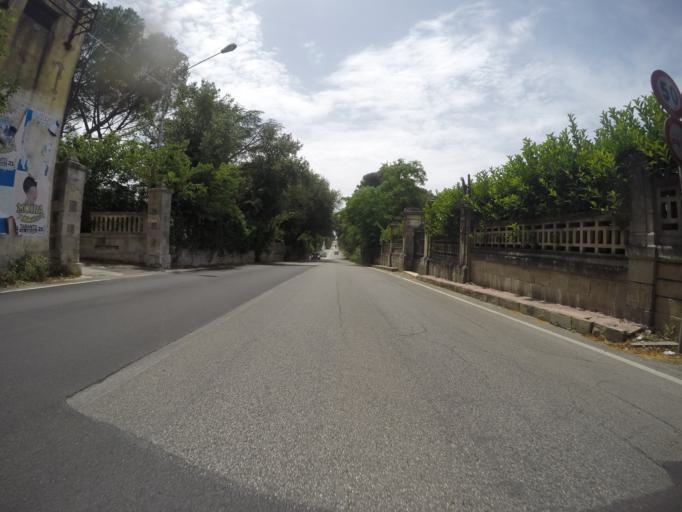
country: IT
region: Apulia
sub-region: Provincia di Taranto
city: Martina Franca
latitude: 40.6945
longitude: 17.3361
